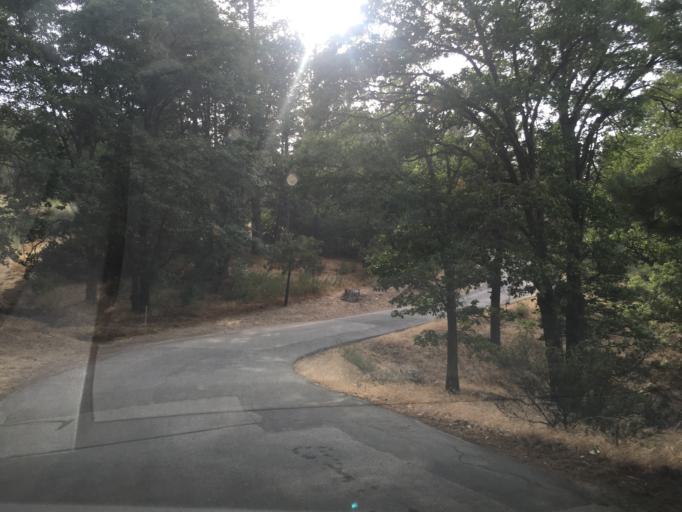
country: US
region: California
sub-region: San Bernardino County
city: Crestline
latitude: 34.2516
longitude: -117.2749
